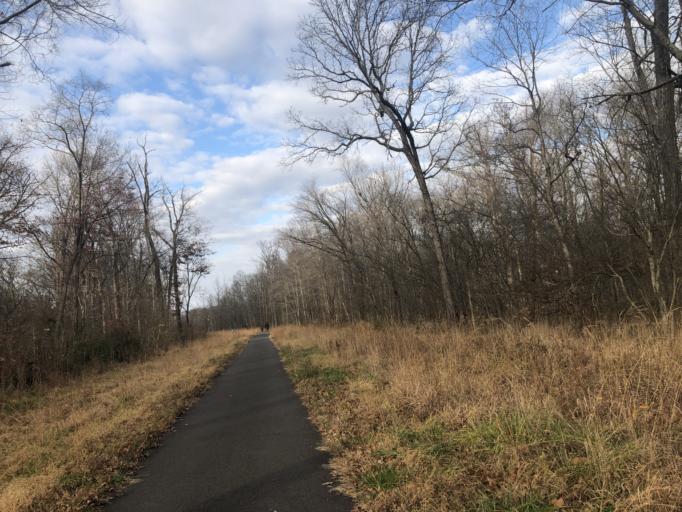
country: US
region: Virginia
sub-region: Fairfax County
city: Centreville
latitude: 38.8508
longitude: -77.4768
